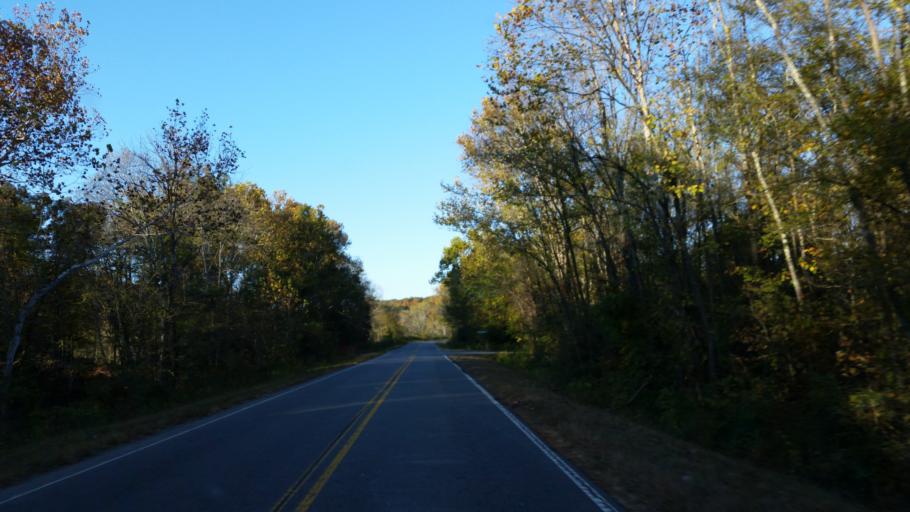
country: US
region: Georgia
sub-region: Bartow County
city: Adairsville
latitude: 34.2719
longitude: -84.9564
